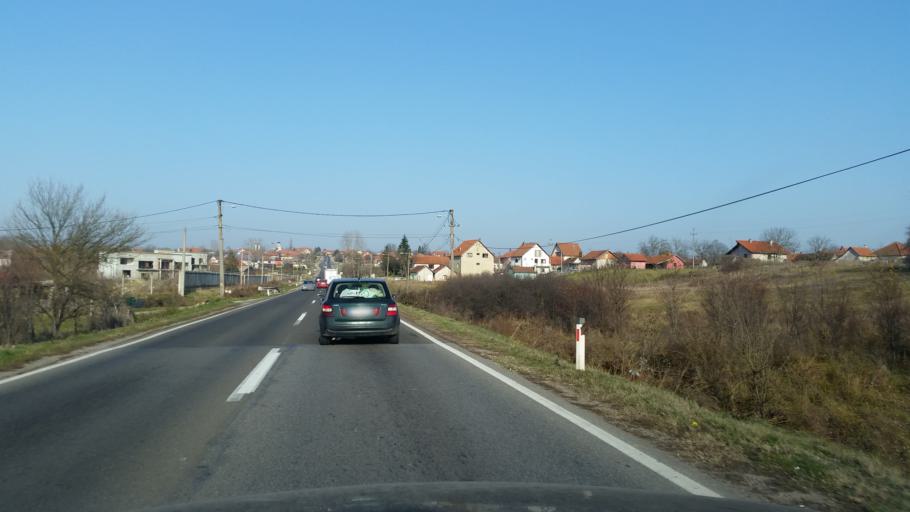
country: RS
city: Stepojevac
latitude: 44.5008
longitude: 20.2899
